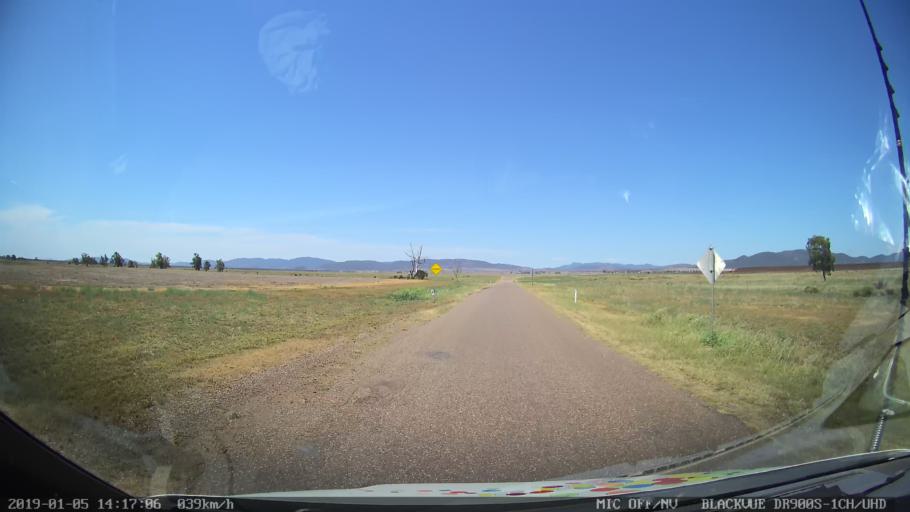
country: AU
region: New South Wales
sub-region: Liverpool Plains
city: Quirindi
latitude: -31.2555
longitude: 150.4745
